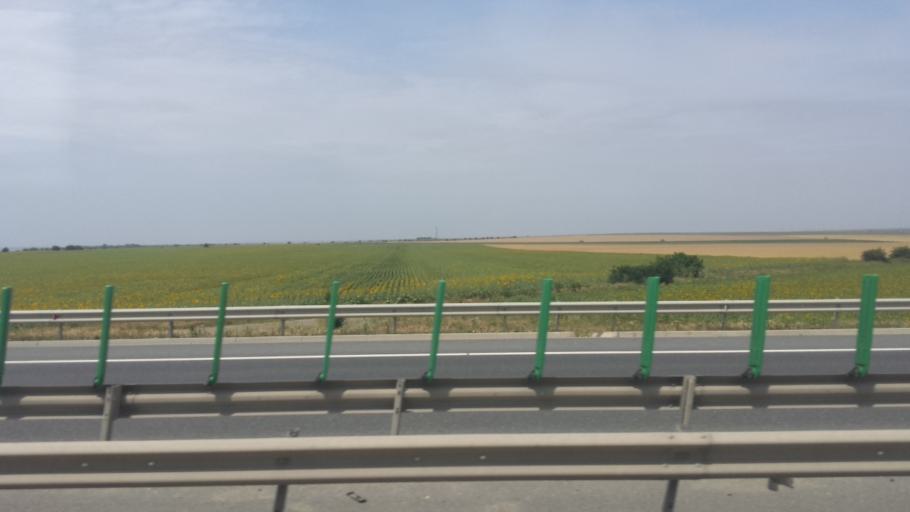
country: RO
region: Constanta
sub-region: Municipiul Constanta
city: Palazu Mare
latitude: 44.1945
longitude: 28.5518
